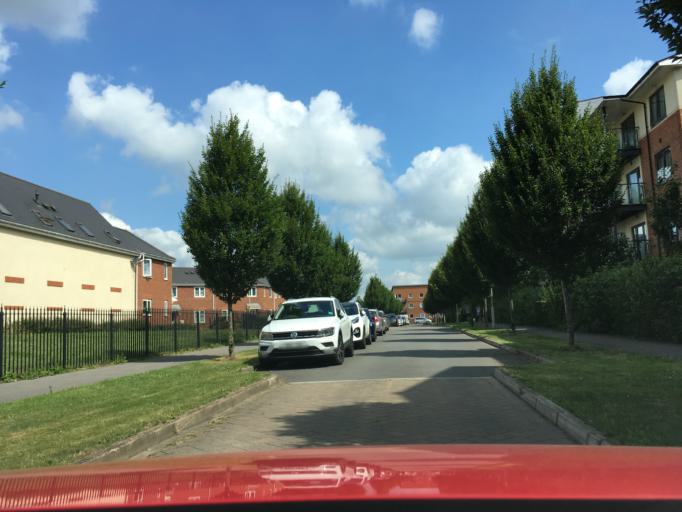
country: GB
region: England
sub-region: Gloucestershire
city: Gloucester
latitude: 51.8740
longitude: -2.2520
